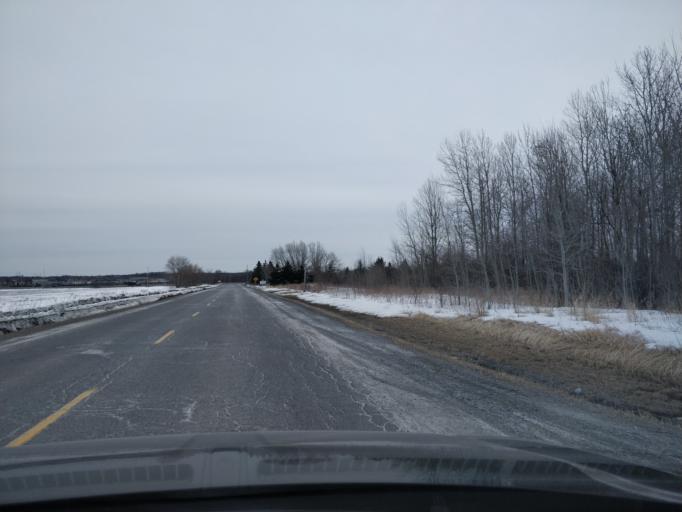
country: CA
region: Ontario
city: Bells Corners
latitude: 45.2638
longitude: -75.8602
